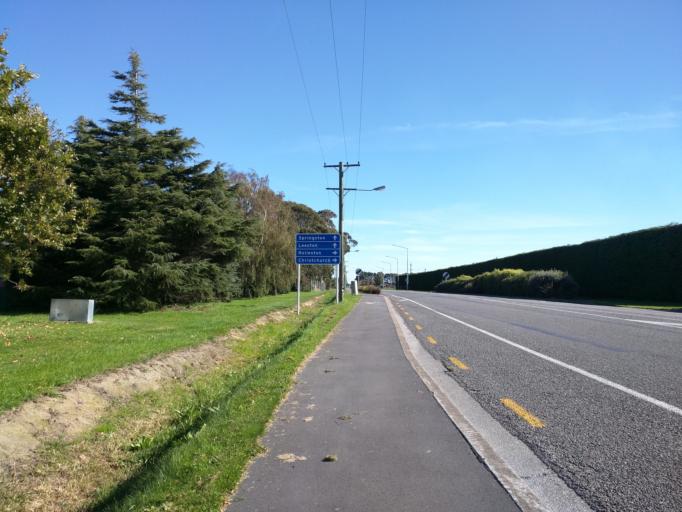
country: NZ
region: Canterbury
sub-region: Selwyn District
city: Lincoln
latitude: -43.6432
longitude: 172.4601
